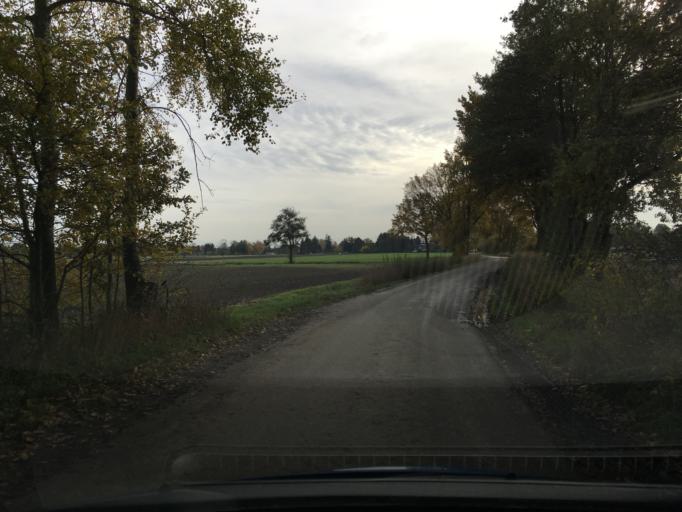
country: DE
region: Lower Saxony
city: Brietlingen
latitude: 53.3575
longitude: 10.4434
